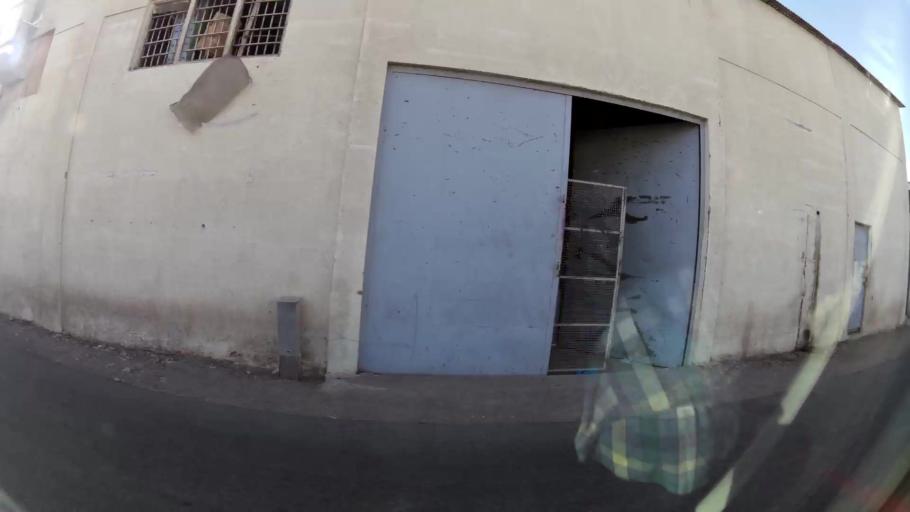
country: OM
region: Muhafazat Masqat
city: Muscat
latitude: 23.5861
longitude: 58.5533
